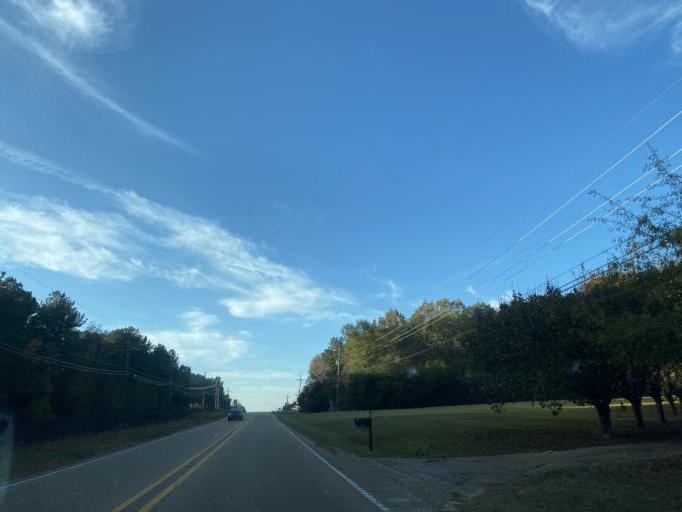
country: US
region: Mississippi
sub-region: Madison County
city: Madison
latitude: 32.4943
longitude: -90.0946
